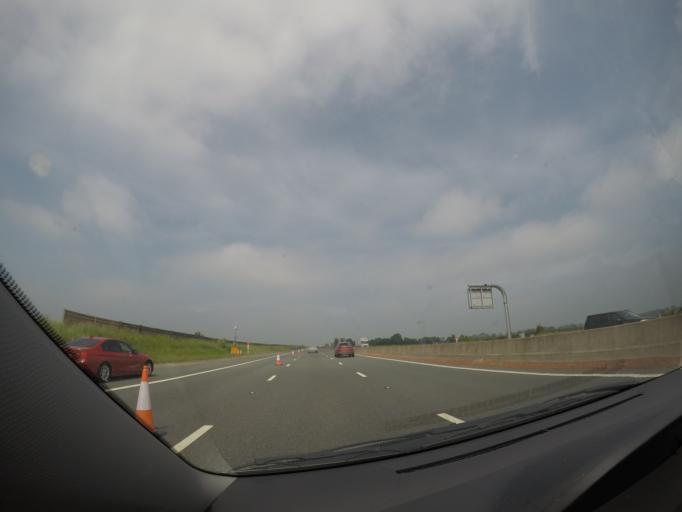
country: GB
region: England
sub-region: North Yorkshire
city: Ripon
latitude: 54.2025
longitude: -1.4721
